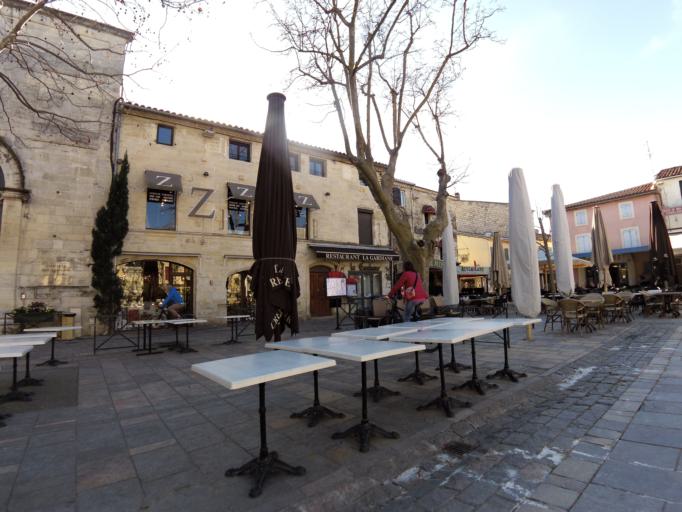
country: FR
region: Languedoc-Roussillon
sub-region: Departement du Gard
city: Aigues-Mortes
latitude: 43.5667
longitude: 4.1901
